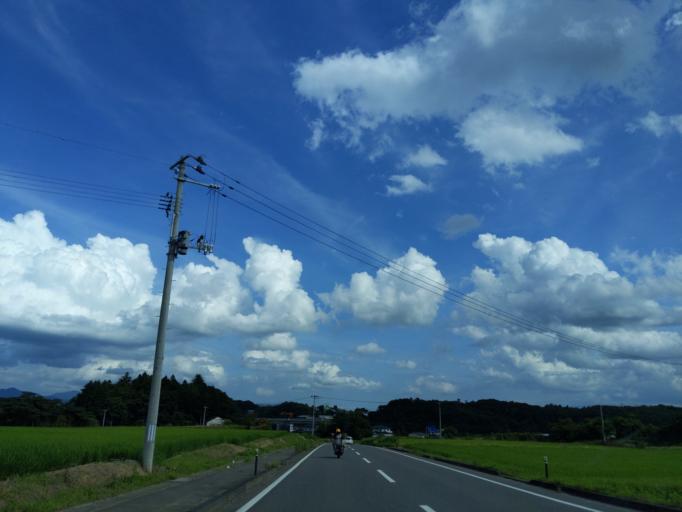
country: JP
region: Fukushima
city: Sukagawa
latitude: 37.3266
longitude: 140.3511
